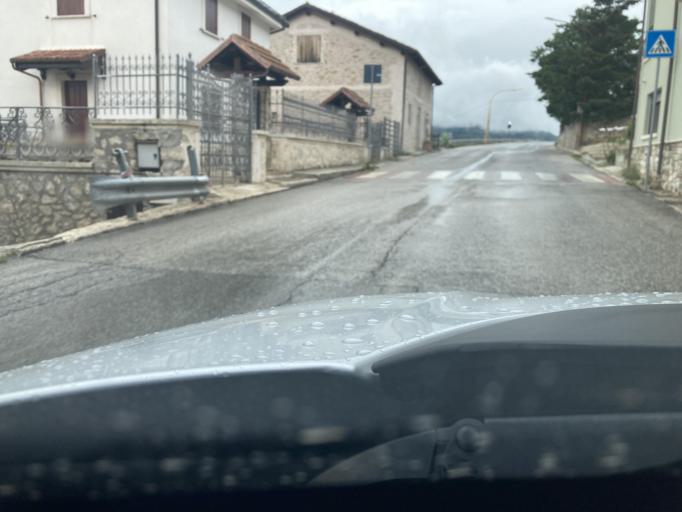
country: IT
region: Abruzzo
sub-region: Provincia dell' Aquila
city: Rocca di Mezzo
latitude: 42.2354
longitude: 13.5329
